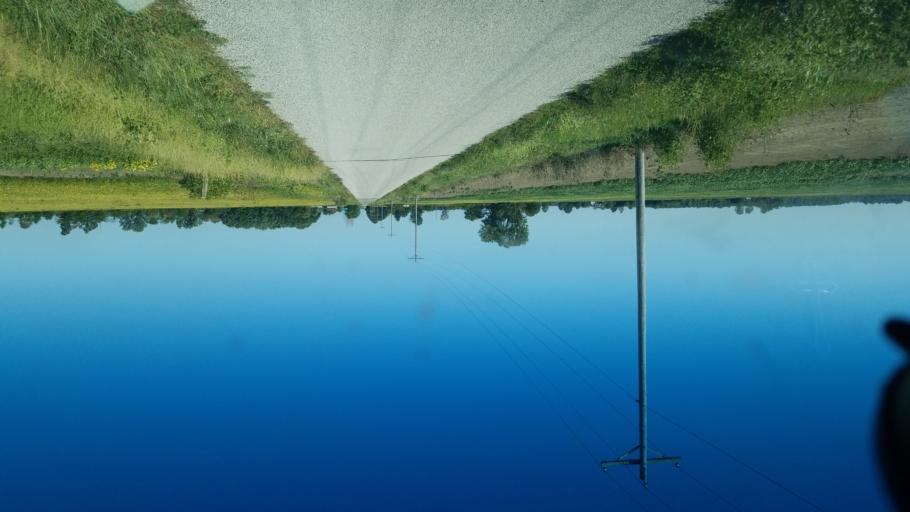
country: US
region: Ohio
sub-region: Marion County
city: Prospect
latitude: 40.4819
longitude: -83.2469
